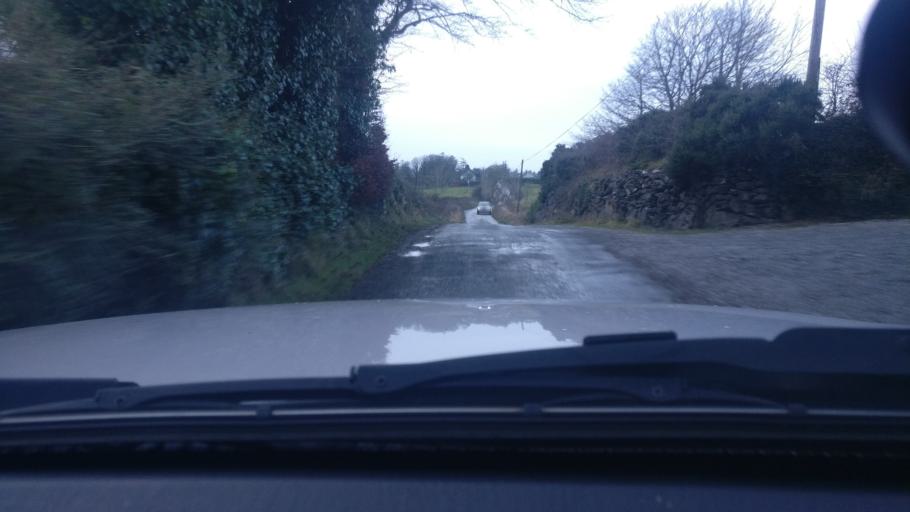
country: IE
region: Connaught
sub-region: County Galway
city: Loughrea
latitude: 53.1639
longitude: -8.5343
